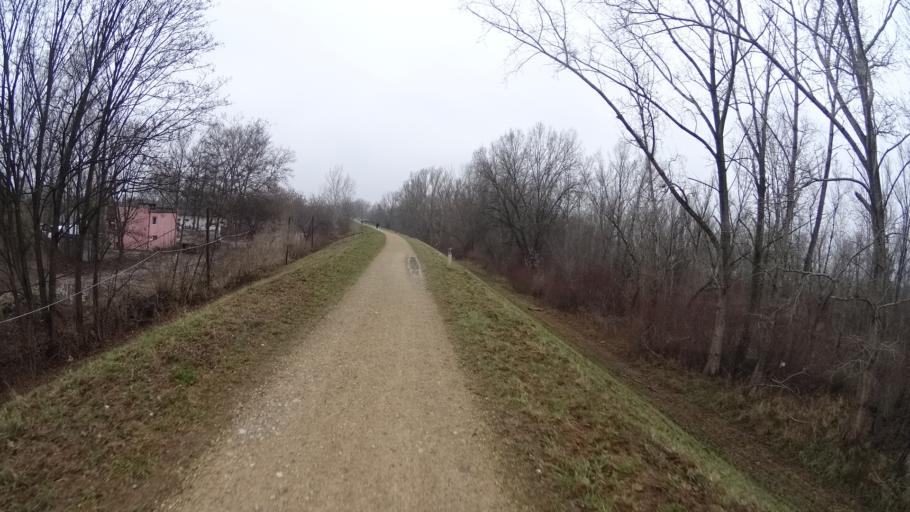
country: PL
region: Masovian Voivodeship
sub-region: Warszawa
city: Praga Poludnie
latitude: 52.2089
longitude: 21.0923
